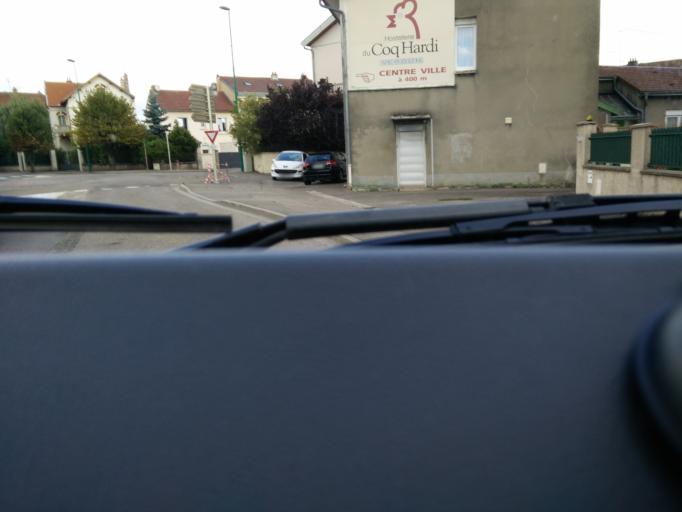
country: FR
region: Lorraine
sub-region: Departement de la Meuse
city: Verdun
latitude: 49.1609
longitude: 5.3931
